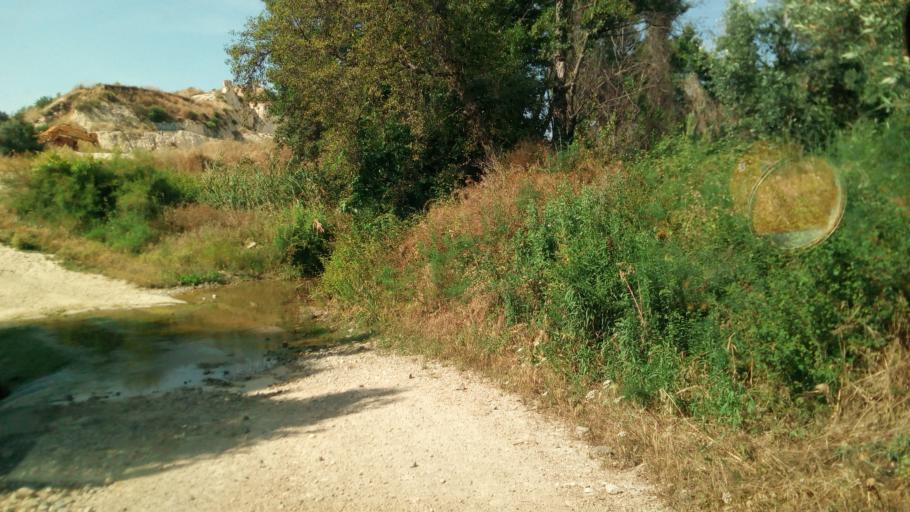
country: CY
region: Pafos
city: Polis
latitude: 34.9524
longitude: 32.5206
